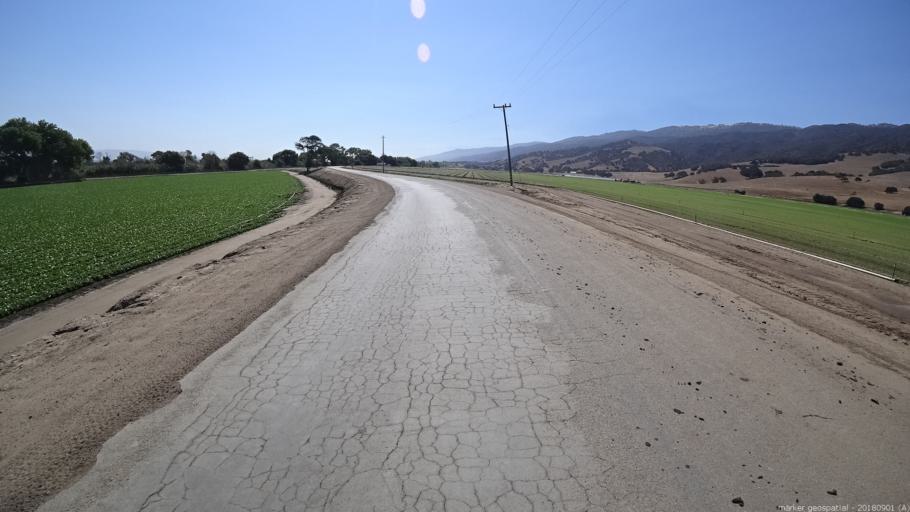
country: US
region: California
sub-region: Monterey County
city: Chualar
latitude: 36.5427
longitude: -121.5436
